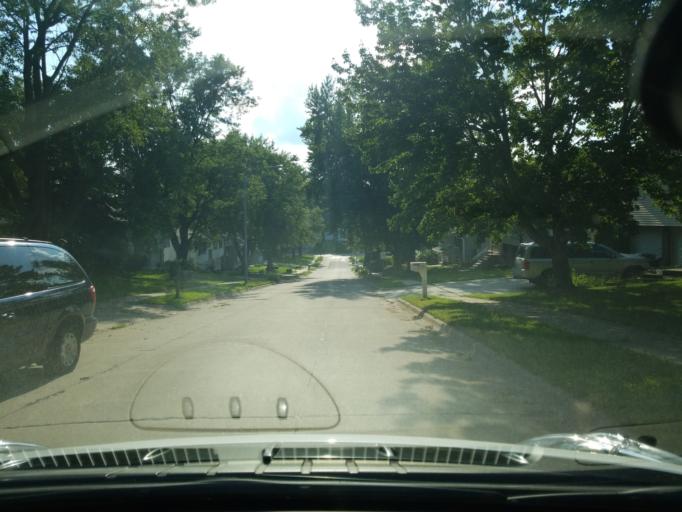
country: US
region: Nebraska
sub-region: Sarpy County
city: Offutt Air Force Base
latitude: 41.1333
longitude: -95.9627
